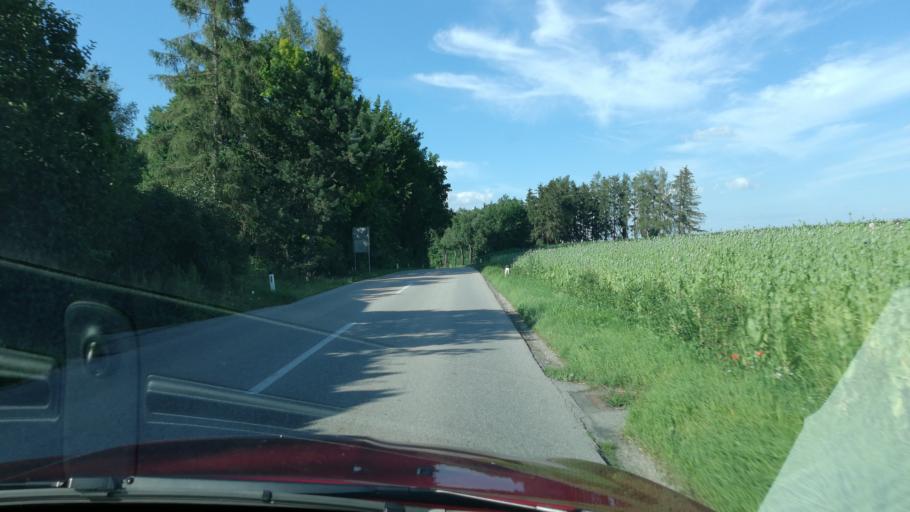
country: AT
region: Upper Austria
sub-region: Politischer Bezirk Steyr-Land
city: Bad Hall
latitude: 48.0183
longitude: 14.2199
